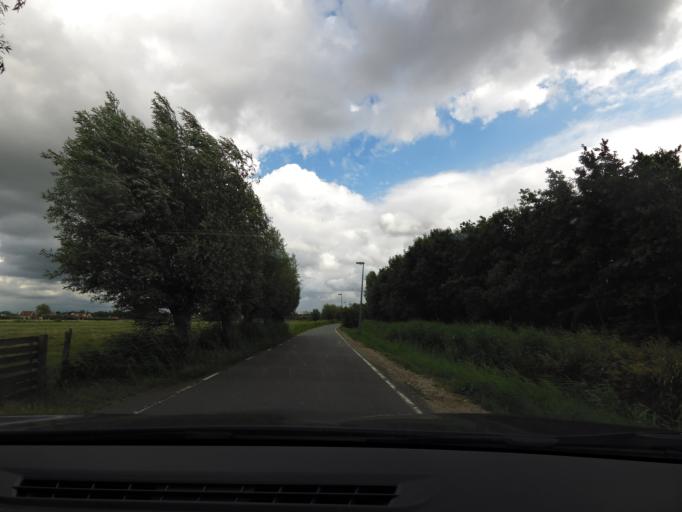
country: NL
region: South Holland
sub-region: Gemeente Vlaardingen
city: Vlaardingen
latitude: 51.9449
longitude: 4.3436
